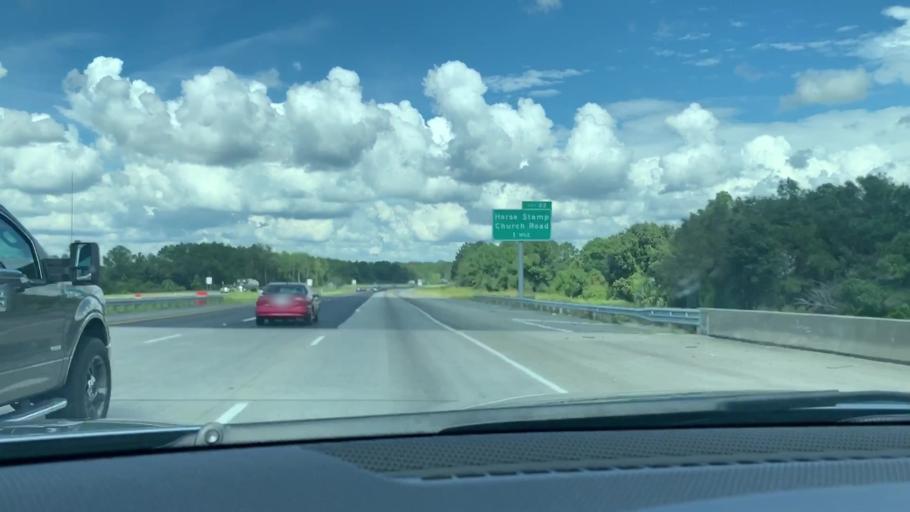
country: US
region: Georgia
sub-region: Camden County
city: Woodbine
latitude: 31.0385
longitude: -81.6527
